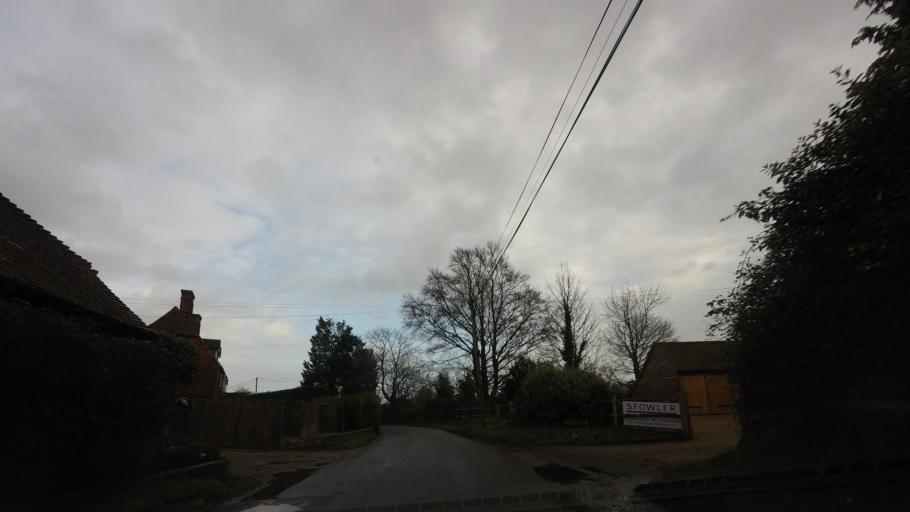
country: GB
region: England
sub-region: Kent
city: Hadlow
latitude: 51.2221
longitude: 0.3202
